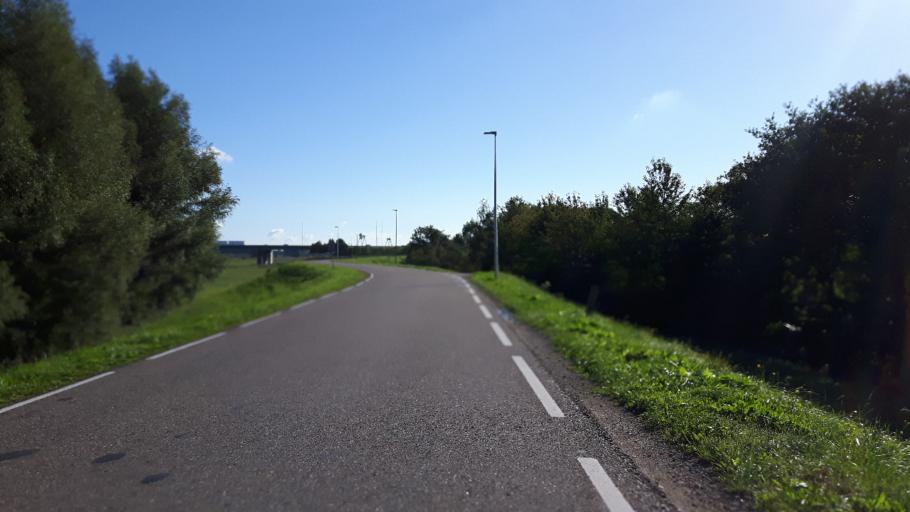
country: NL
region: Utrecht
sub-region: Gemeente Vianen
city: Vianen
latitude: 51.9975
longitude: 5.1052
